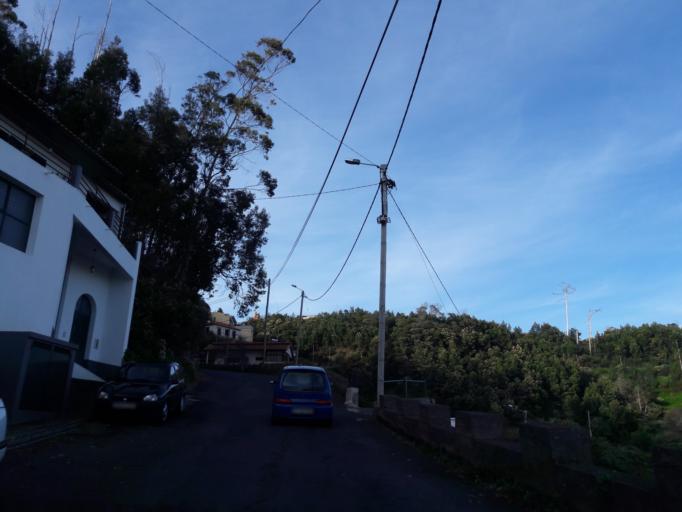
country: PT
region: Madeira
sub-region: Santa Cruz
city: Camacha
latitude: 32.6658
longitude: -16.8454
